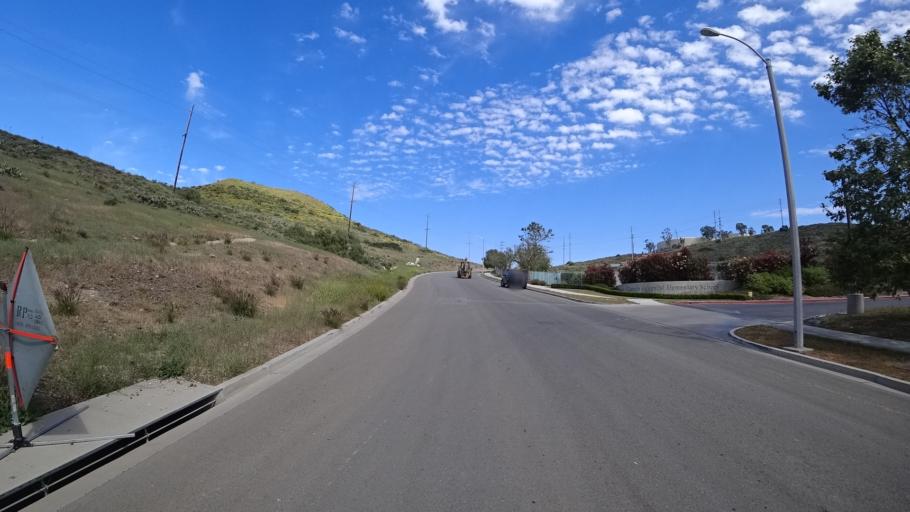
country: US
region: California
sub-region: Ventura County
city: Casa Conejo
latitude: 34.1949
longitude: -118.9377
